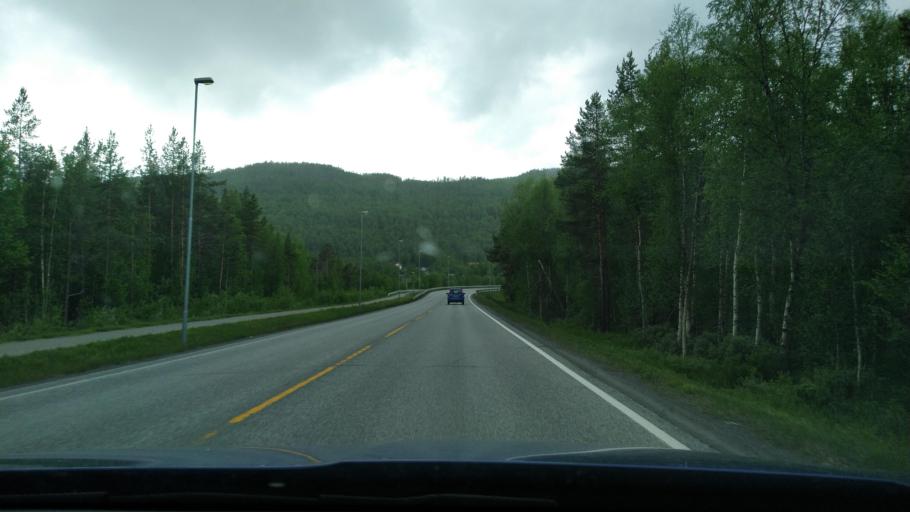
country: NO
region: Troms
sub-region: Malselv
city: Moen
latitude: 69.0099
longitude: 18.4932
